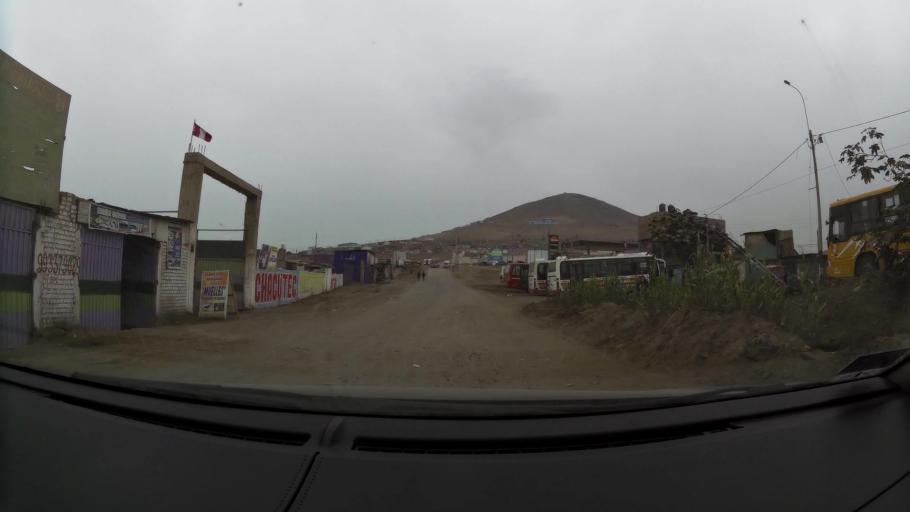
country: PE
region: Lima
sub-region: Lima
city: Santa Rosa
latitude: -11.8319
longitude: -77.1678
